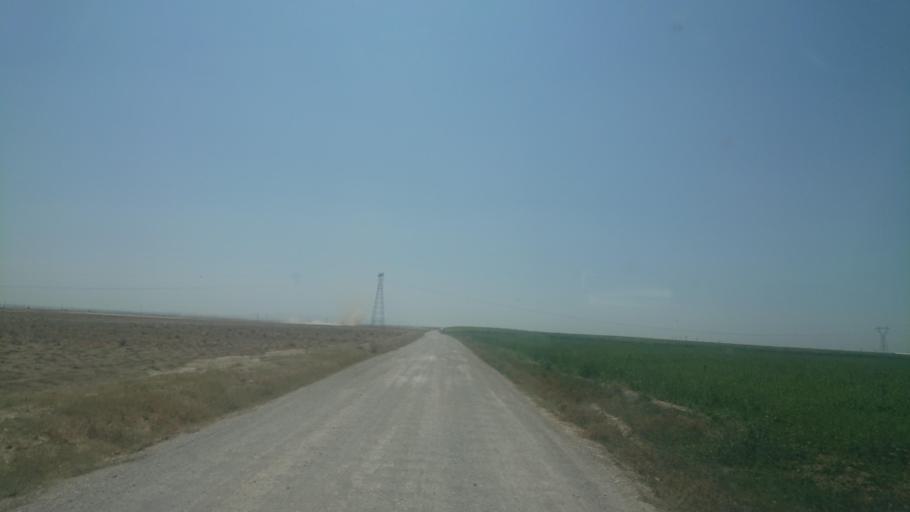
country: TR
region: Aksaray
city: Sultanhani
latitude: 38.2520
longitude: 33.6514
